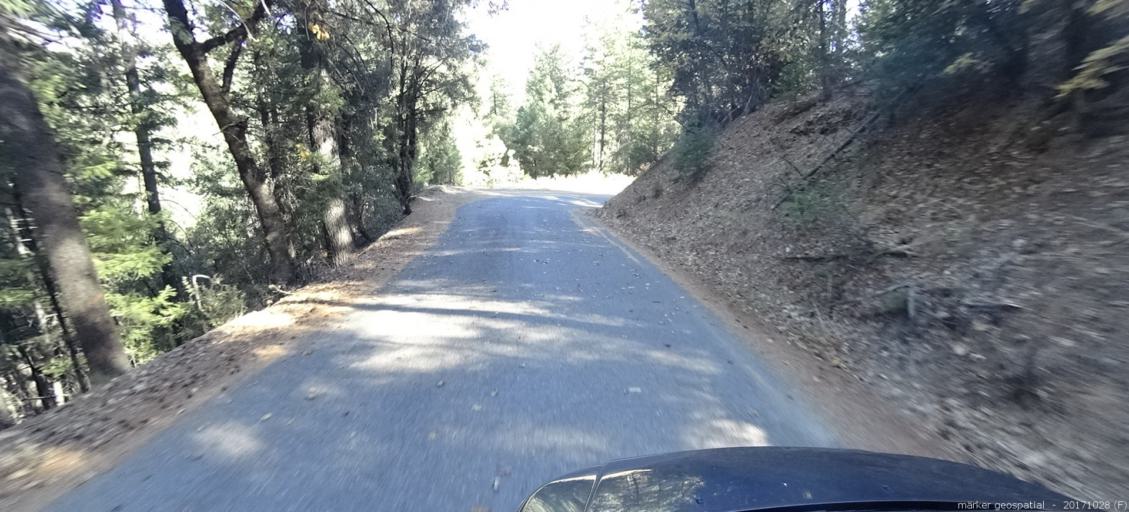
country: US
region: California
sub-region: Trinity County
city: Lewiston
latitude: 40.8154
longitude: -122.6397
